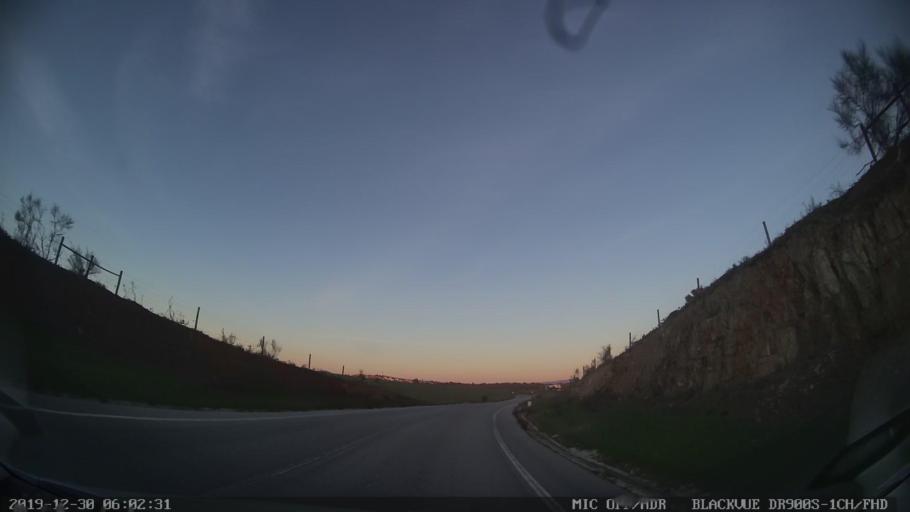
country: PT
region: Castelo Branco
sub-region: Penamacor
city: Penamacor
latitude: 40.0708
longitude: -7.2432
